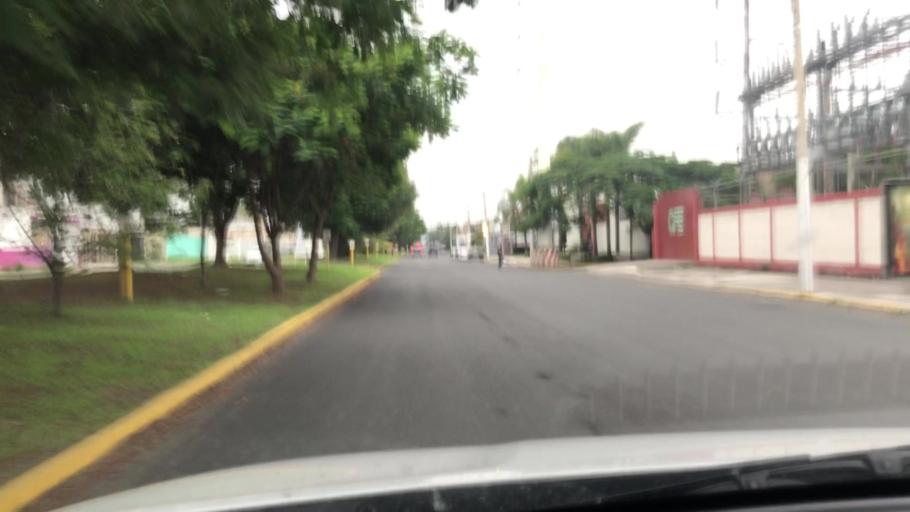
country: MX
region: Jalisco
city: Guadalajara
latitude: 20.6413
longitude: -103.4301
